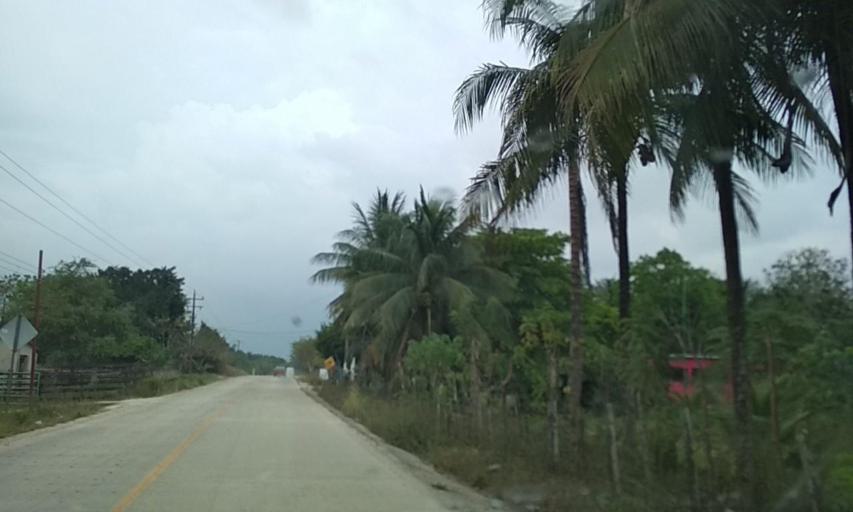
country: MX
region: Tabasco
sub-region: Huimanguillo
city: Francisco Rueda
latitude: 17.7187
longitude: -94.0945
